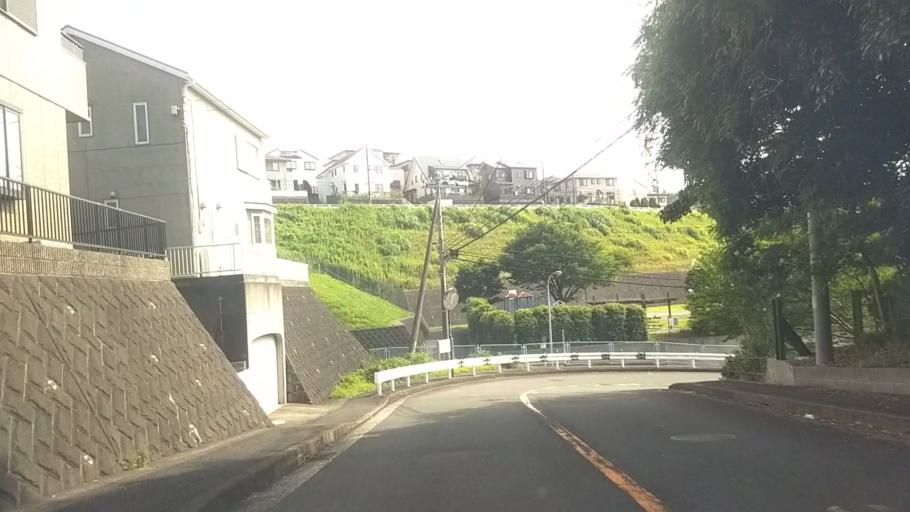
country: JP
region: Kanagawa
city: Yokosuka
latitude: 35.2482
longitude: 139.7038
